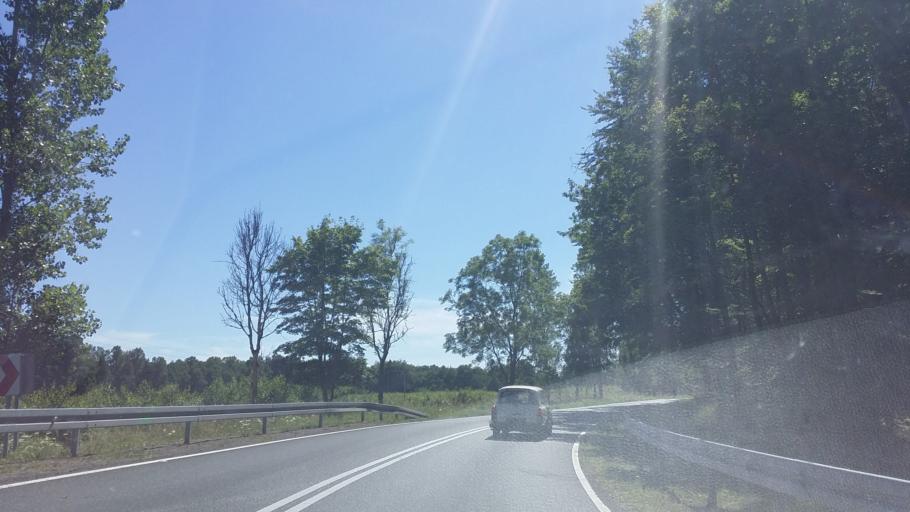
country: PL
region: West Pomeranian Voivodeship
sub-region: Powiat stargardzki
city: Insko
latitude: 53.4805
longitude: 15.5819
